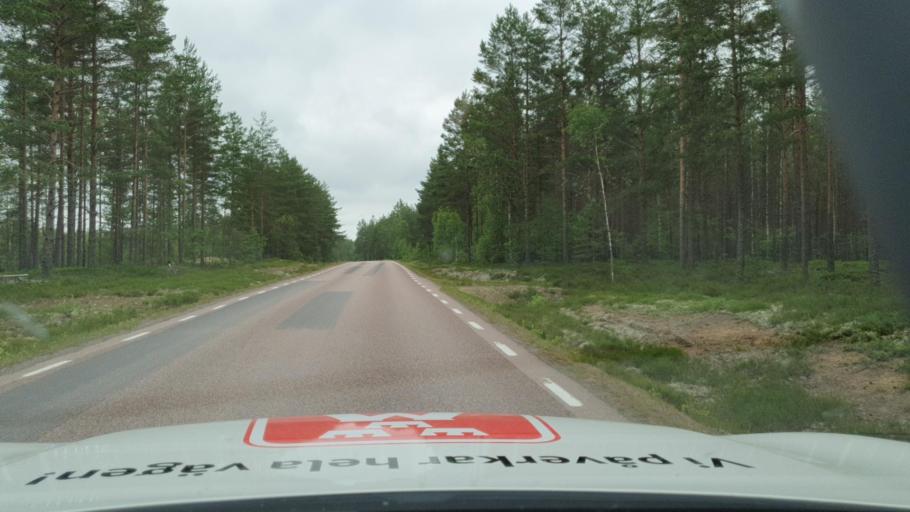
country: SE
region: Vaermland
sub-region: Kristinehamns Kommun
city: Kristinehamn
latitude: 59.5112
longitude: 13.9525
